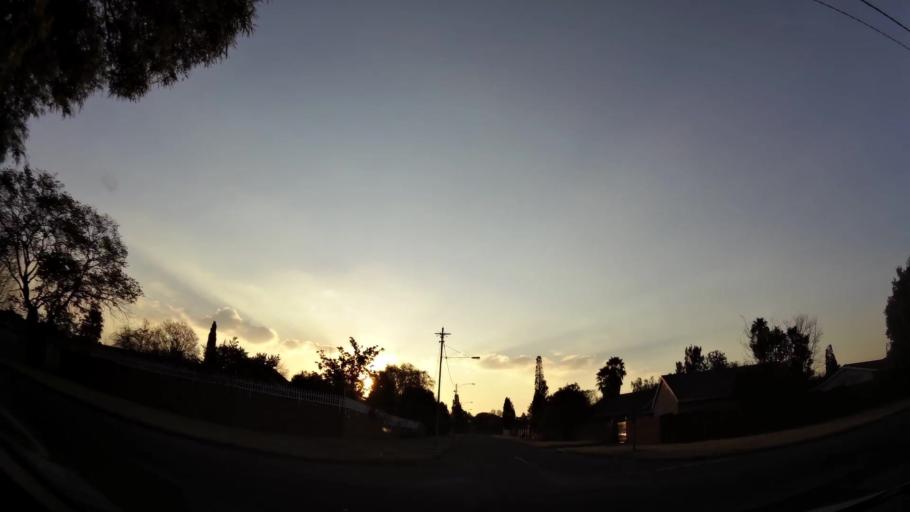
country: ZA
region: Gauteng
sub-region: Ekurhuleni Metropolitan Municipality
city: Springs
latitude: -26.3116
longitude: 28.4508
